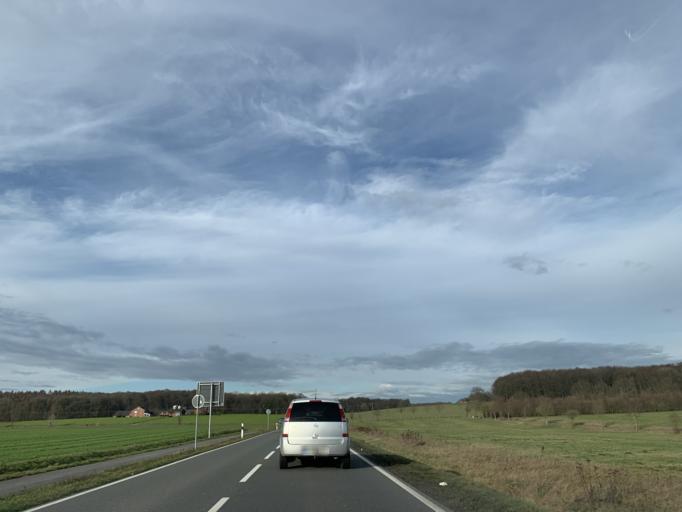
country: DE
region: North Rhine-Westphalia
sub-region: Regierungsbezirk Munster
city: Nottuln
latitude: 51.9339
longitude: 7.3405
